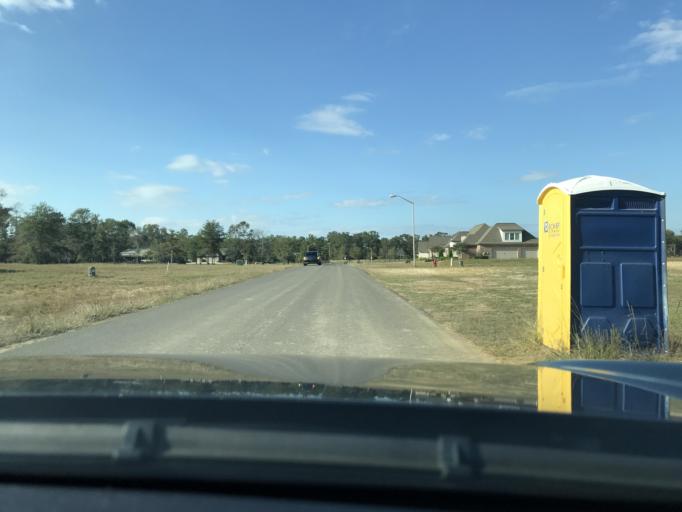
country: US
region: Louisiana
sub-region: Calcasieu Parish
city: Moss Bluff
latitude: 30.3374
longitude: -93.2517
